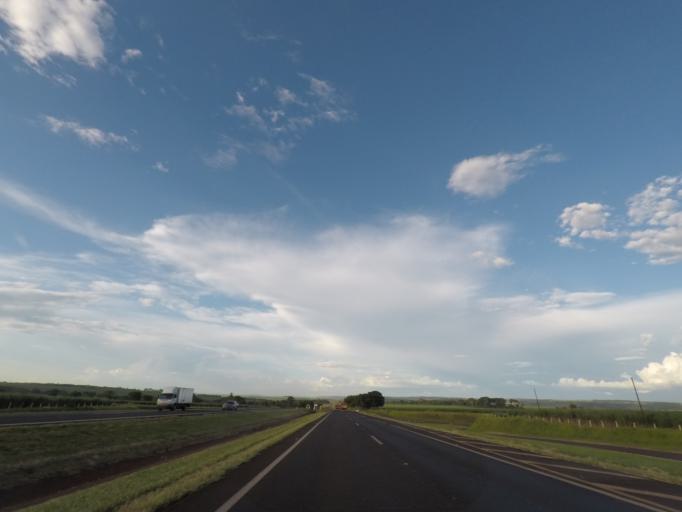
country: BR
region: Sao Paulo
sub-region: Ituverava
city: Ituverava
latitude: -20.3211
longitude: -47.8029
